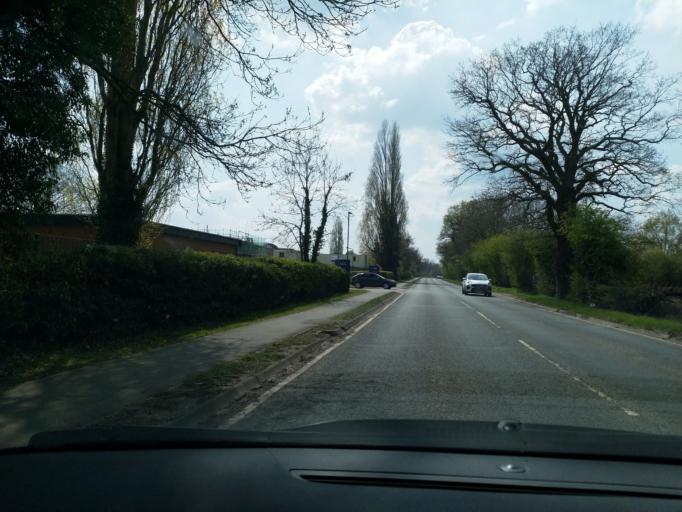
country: GB
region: England
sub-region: Warwickshire
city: Ryton on Dunsmore
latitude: 52.3567
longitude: -1.4414
